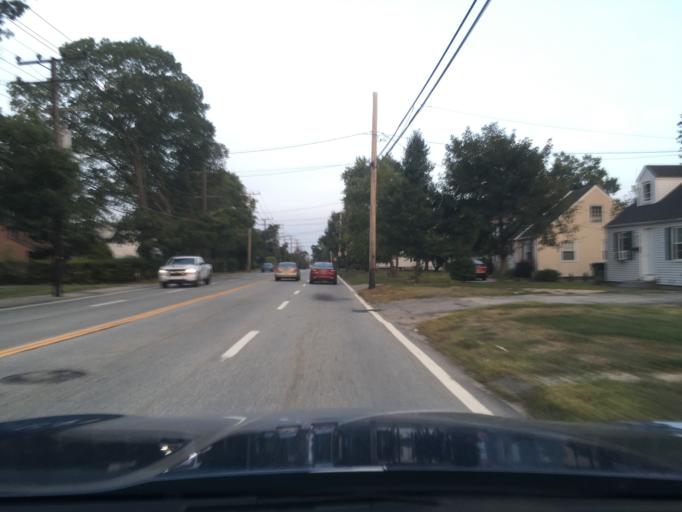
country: US
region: Rhode Island
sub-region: Kent County
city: Warwick
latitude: 41.7159
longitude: -71.4604
